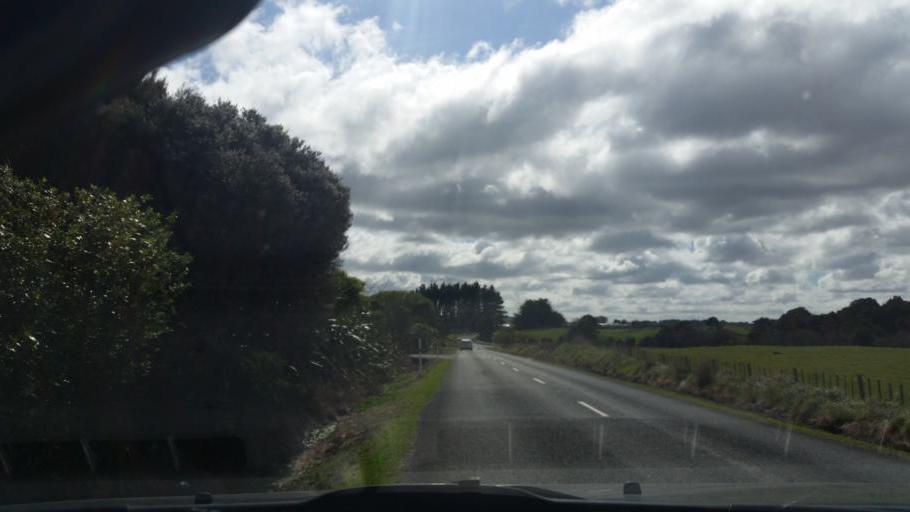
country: NZ
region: Auckland
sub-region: Auckland
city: Wellsford
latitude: -36.1503
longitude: 174.5028
